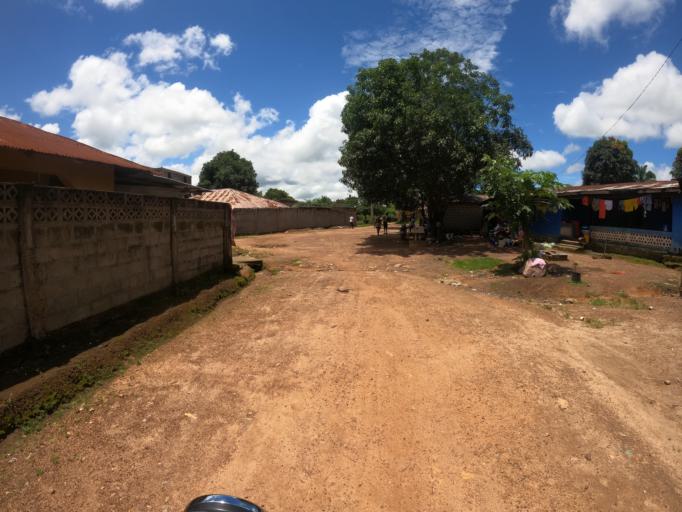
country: SL
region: Northern Province
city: Makeni
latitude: 8.8918
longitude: -12.0652
